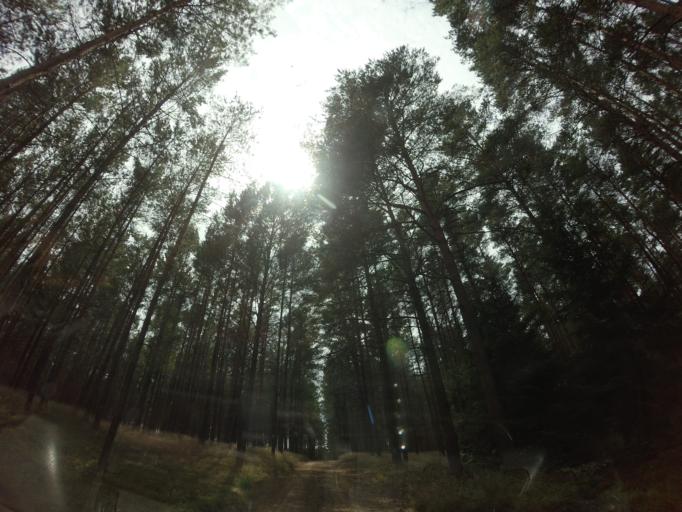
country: PL
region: West Pomeranian Voivodeship
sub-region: Powiat choszczenski
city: Drawno
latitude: 53.1647
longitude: 15.7841
